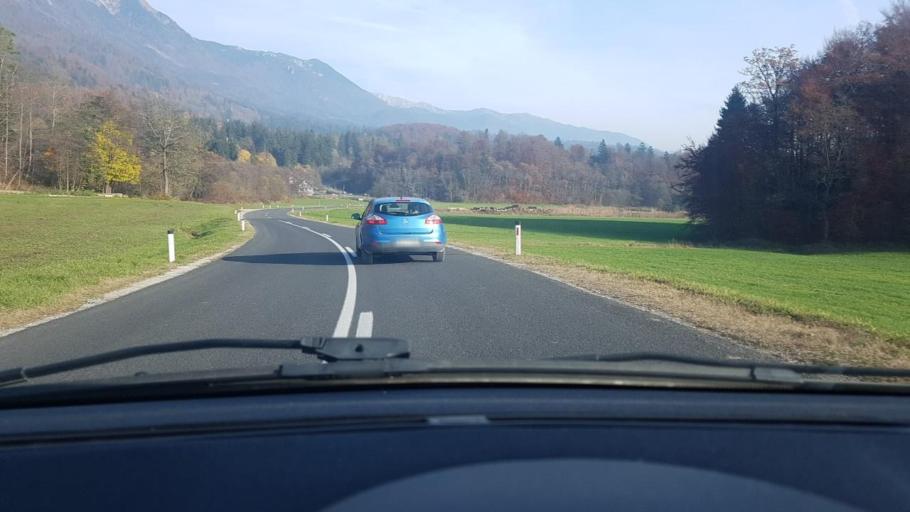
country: SI
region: Kranj
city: Golnik
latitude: 46.3272
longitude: 14.3210
